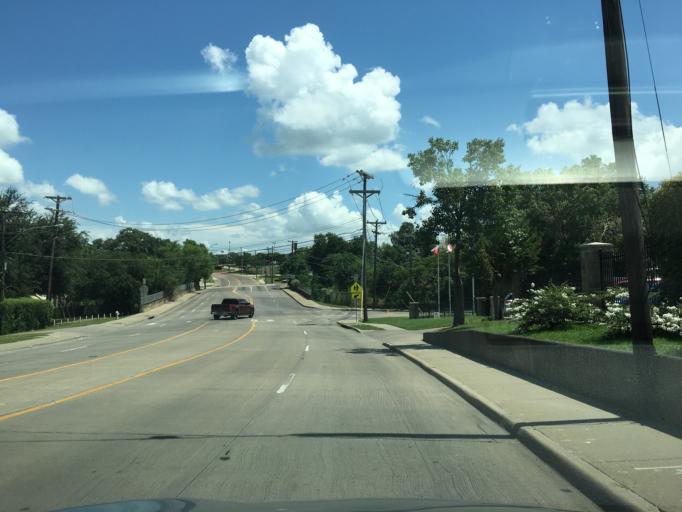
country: US
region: Texas
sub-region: Dallas County
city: Highland Park
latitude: 32.8644
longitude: -96.7499
